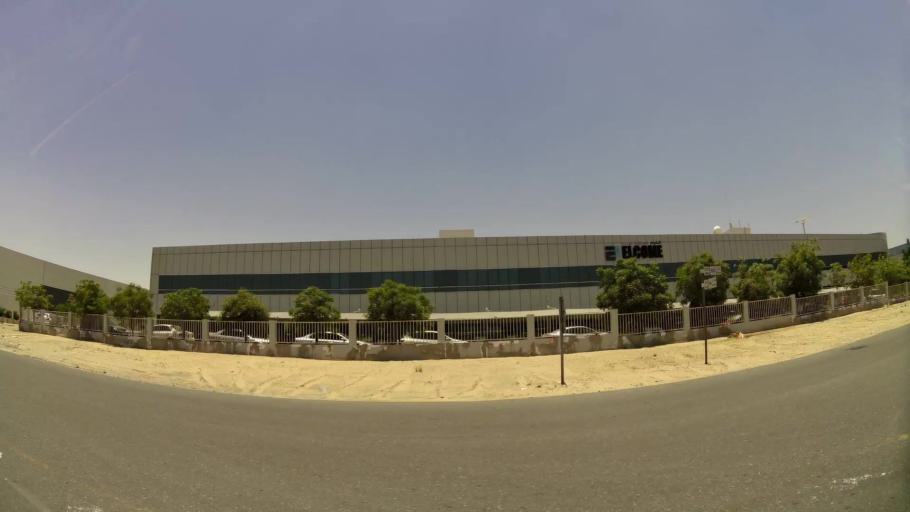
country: AE
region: Dubai
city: Dubai
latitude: 24.9818
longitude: 55.1732
